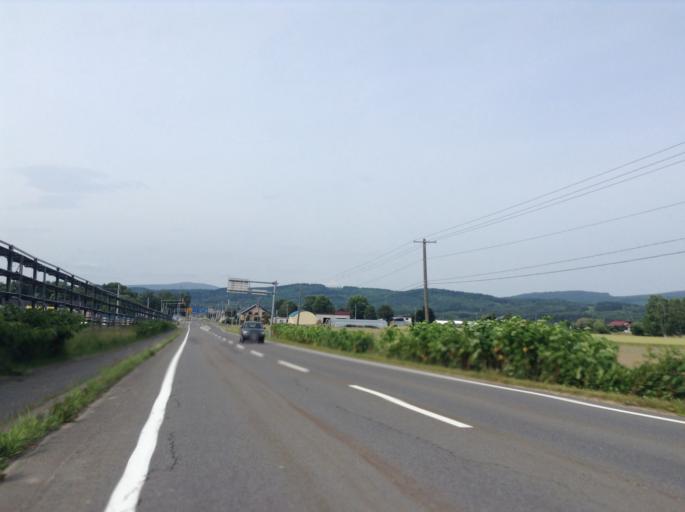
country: JP
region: Hokkaido
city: Nayoro
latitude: 44.4339
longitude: 142.4021
